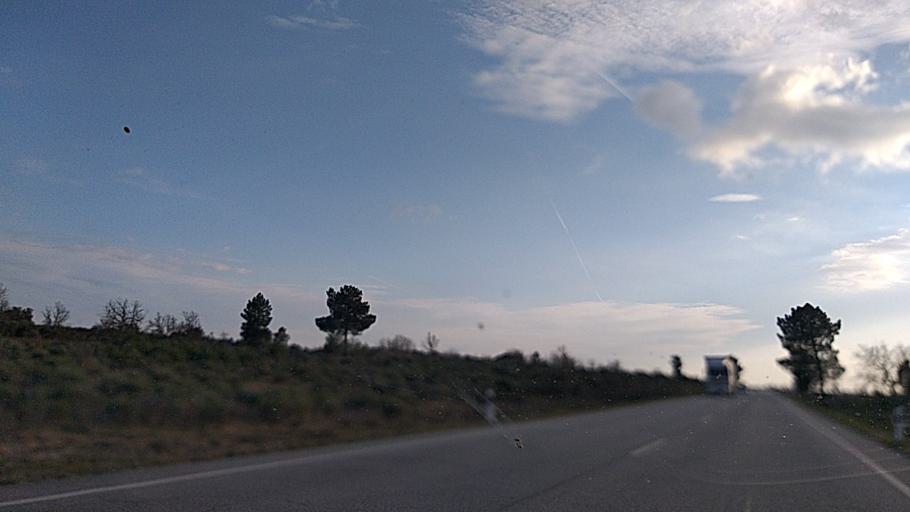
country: ES
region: Castille and Leon
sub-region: Provincia de Salamanca
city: Fuentes de Onoro
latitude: 40.6243
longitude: -6.9759
